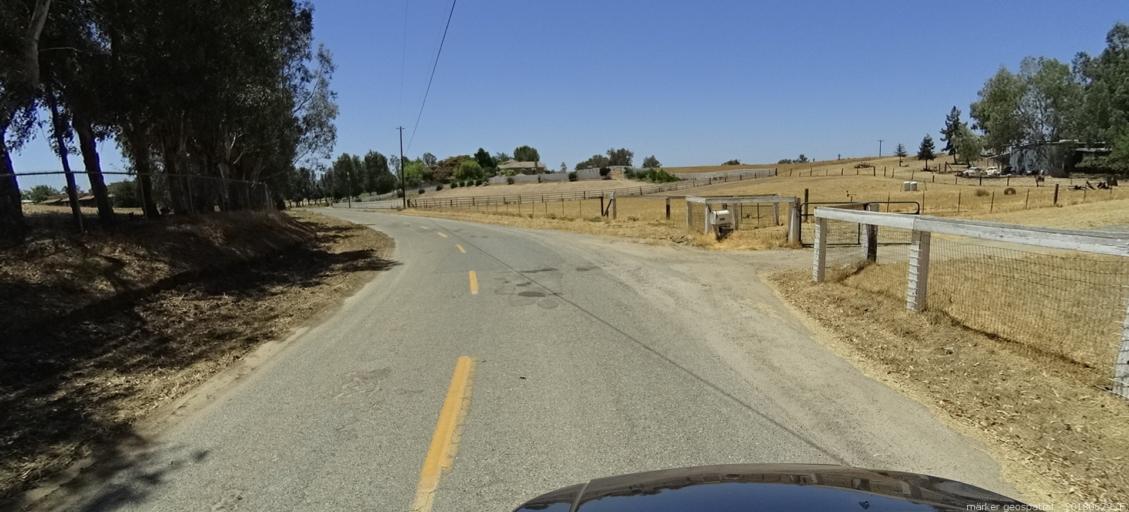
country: US
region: California
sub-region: Madera County
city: Parksdale
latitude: 37.0041
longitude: -119.9779
